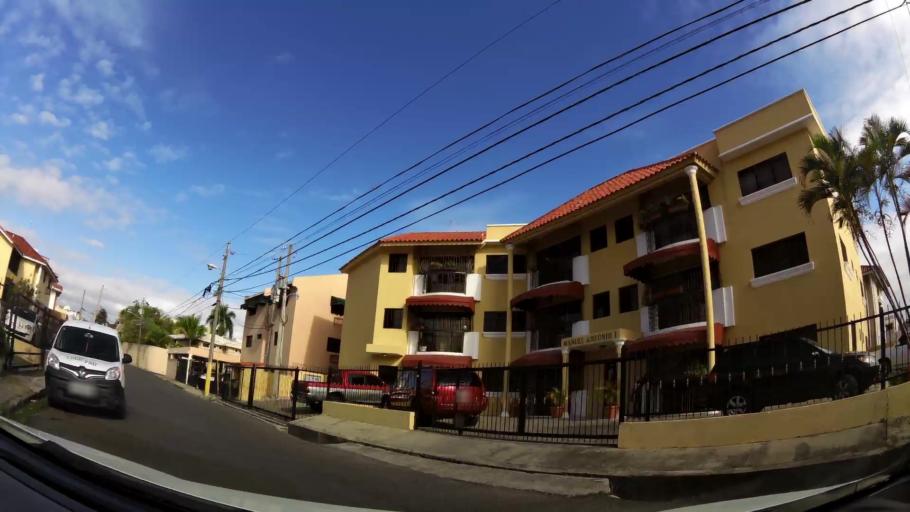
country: DO
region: Nacional
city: La Julia
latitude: 18.4754
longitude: -69.9472
